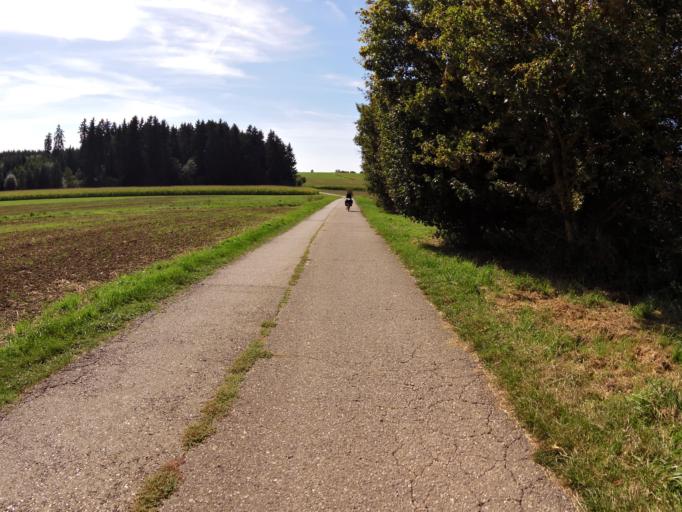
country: DE
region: Baden-Wuerttemberg
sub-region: Freiburg Region
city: Bad Durrheim
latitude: 48.0238
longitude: 8.5004
